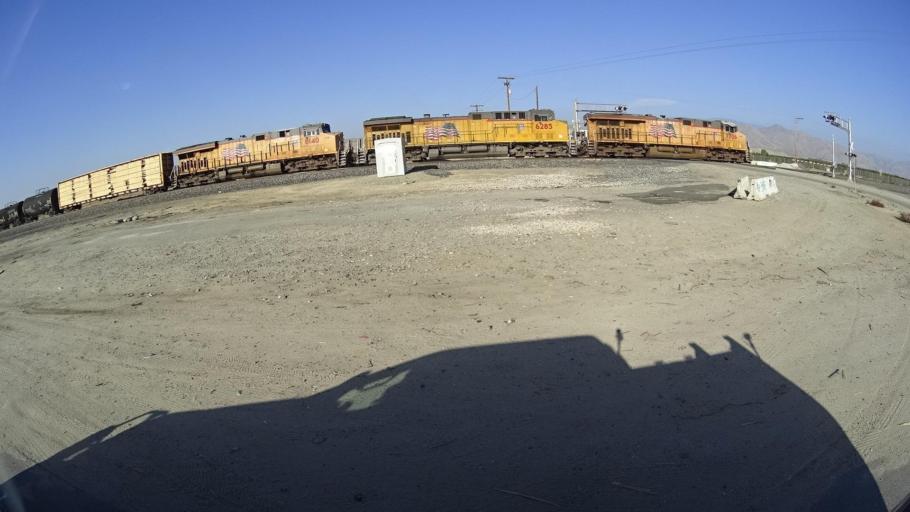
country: US
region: California
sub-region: Kern County
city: Arvin
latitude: 35.3283
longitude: -118.7899
